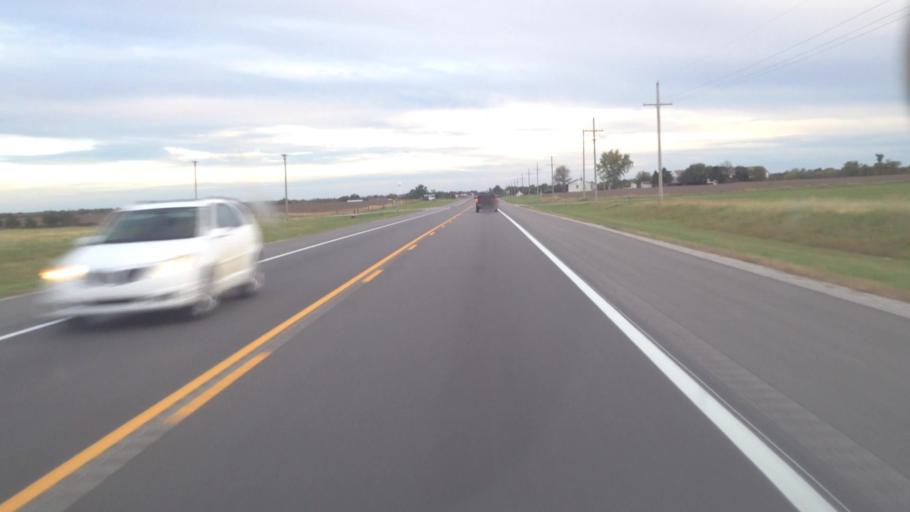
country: US
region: Kansas
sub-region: Franklin County
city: Ottawa
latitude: 38.5081
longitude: -95.2676
